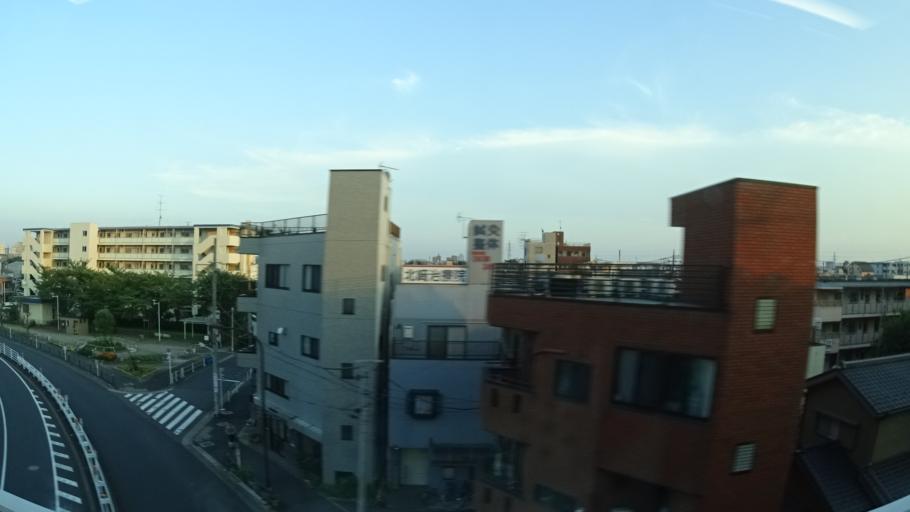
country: JP
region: Saitama
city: Yashio-shi
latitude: 35.7633
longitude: 139.8376
